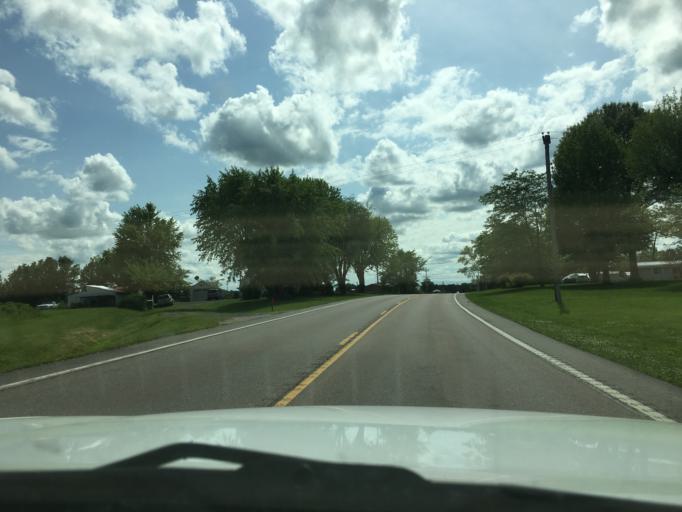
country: US
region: Missouri
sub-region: Franklin County
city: Gerald
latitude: 38.3889
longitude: -91.3750
